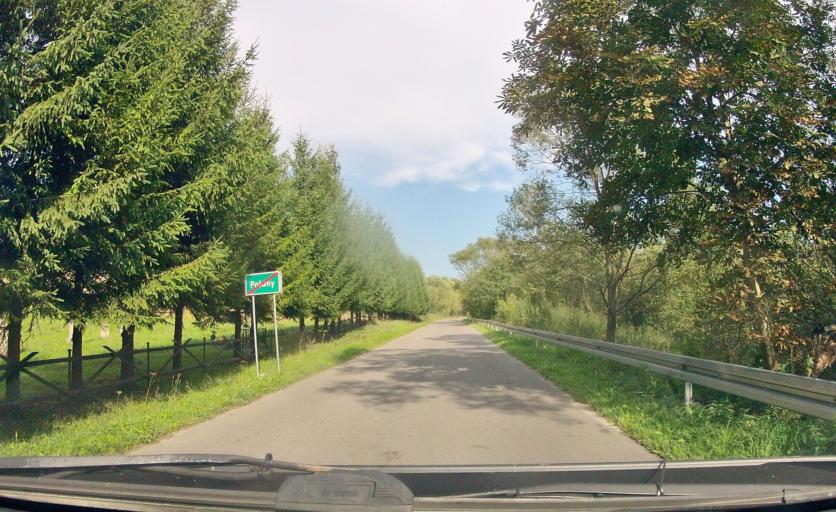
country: PL
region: Subcarpathian Voivodeship
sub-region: Powiat jasielski
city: Krempna
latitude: 49.4966
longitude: 21.5693
